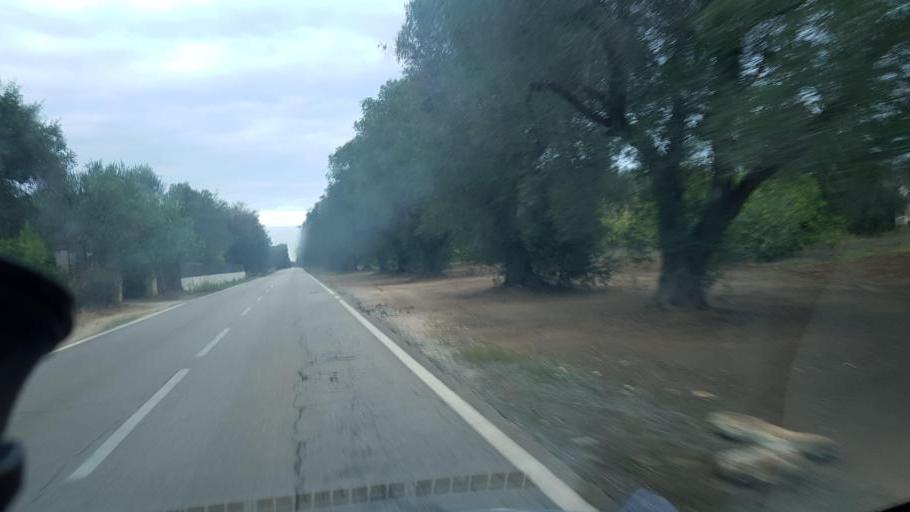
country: IT
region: Apulia
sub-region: Provincia di Brindisi
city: Latiano
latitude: 40.5284
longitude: 17.6854
